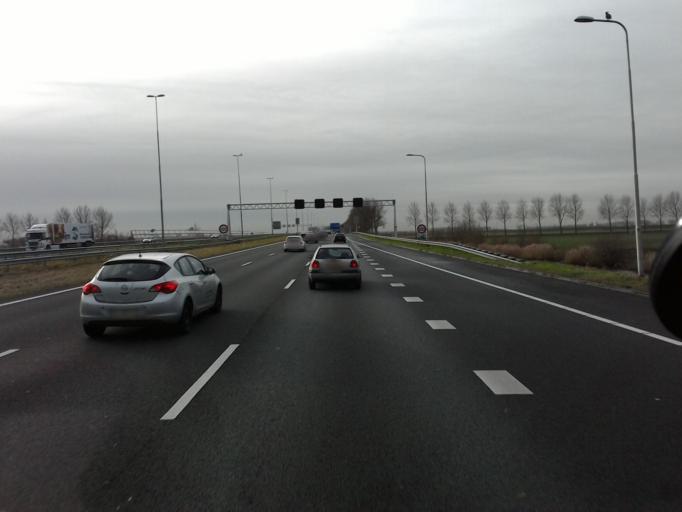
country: NL
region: South Holland
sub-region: Gemeente Kaag en Braassem
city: Oude Wetering
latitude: 52.2285
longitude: 4.6413
